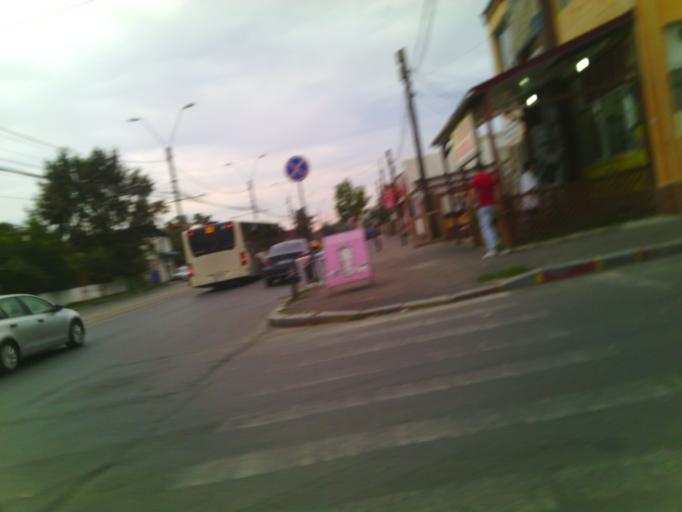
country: RO
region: Ilfov
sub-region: Comuna Jilava
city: Jilava
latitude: 44.3746
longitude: 26.0908
